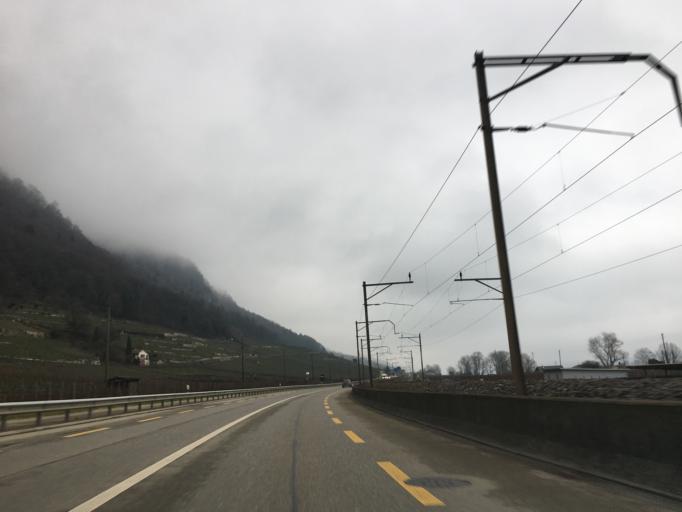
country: CH
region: Bern
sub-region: Jura bernois
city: La Neuveville
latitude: 47.0758
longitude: 7.1153
